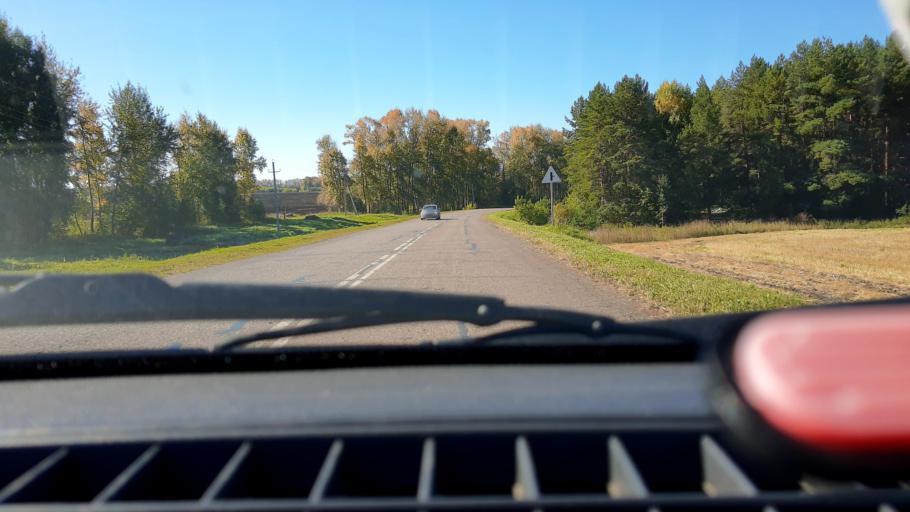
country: RU
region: Bashkortostan
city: Kushnarenkovo
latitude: 55.0646
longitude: 55.4480
